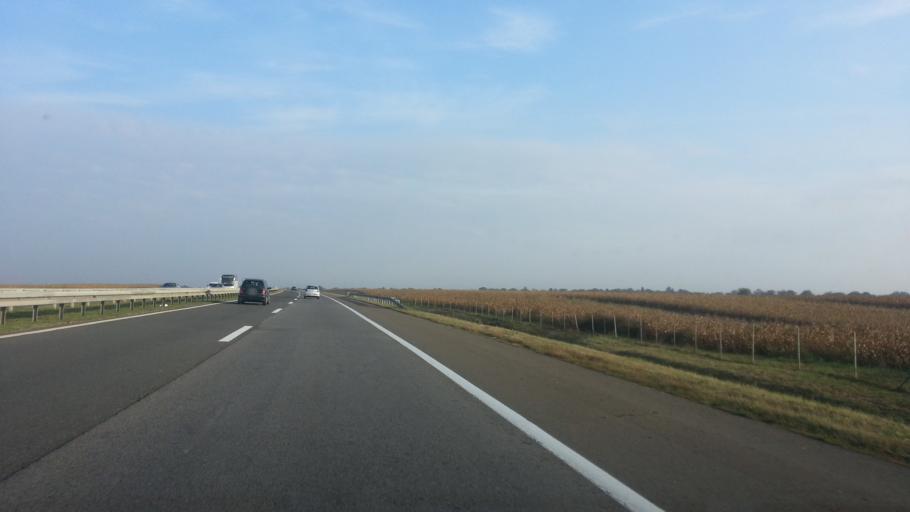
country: RS
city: Novi Banovci
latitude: 44.9228
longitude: 20.3037
